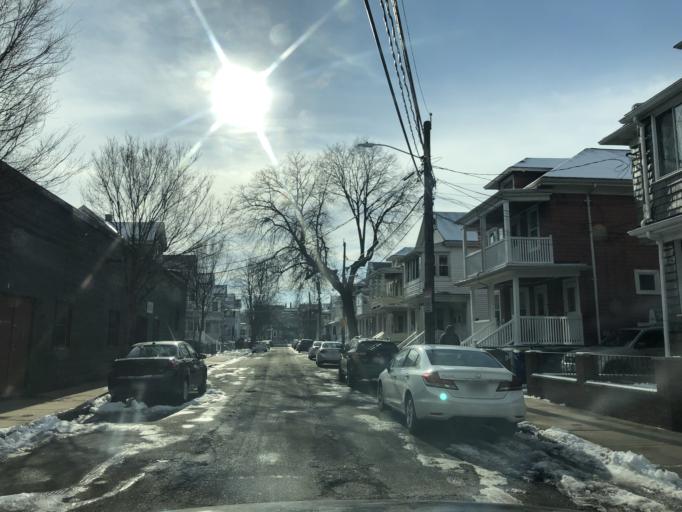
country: US
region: Massachusetts
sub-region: Middlesex County
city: Cambridge
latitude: 42.3792
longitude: -71.1021
